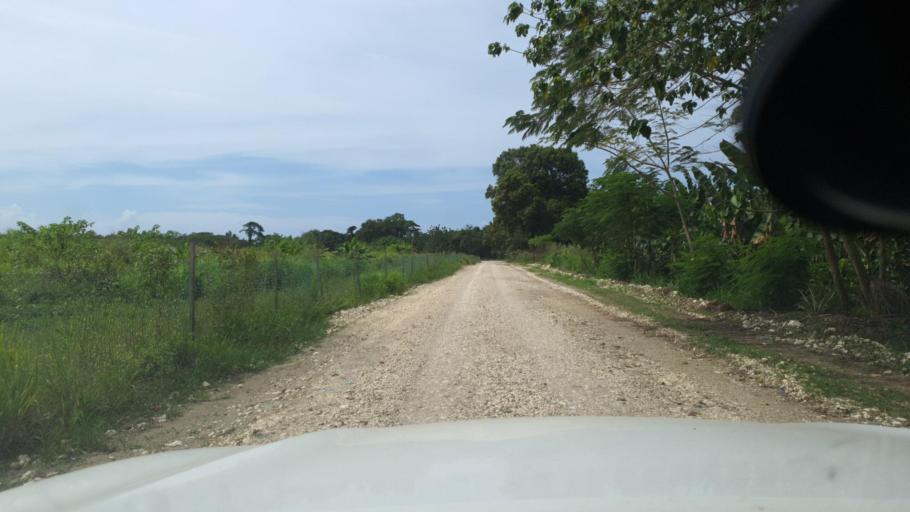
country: SB
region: Guadalcanal
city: Honiara
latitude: -9.4147
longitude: 159.8911
